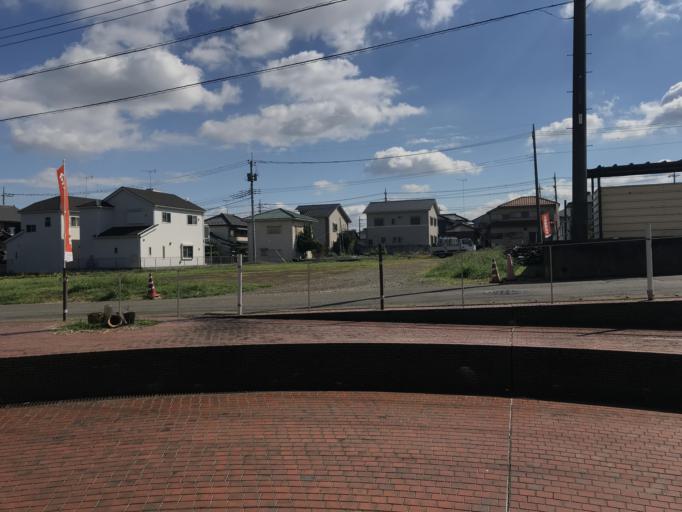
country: JP
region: Tochigi
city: Oyama
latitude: 36.2614
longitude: 139.7556
